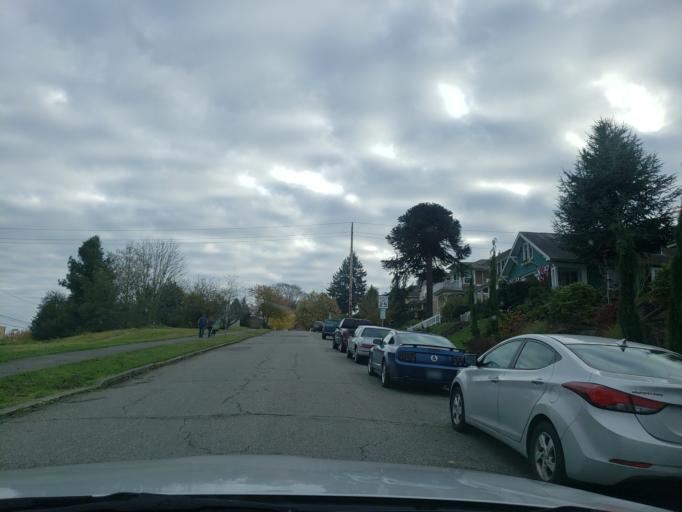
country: US
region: Washington
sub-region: Snohomish County
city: Everett
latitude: 47.9761
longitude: -122.2128
